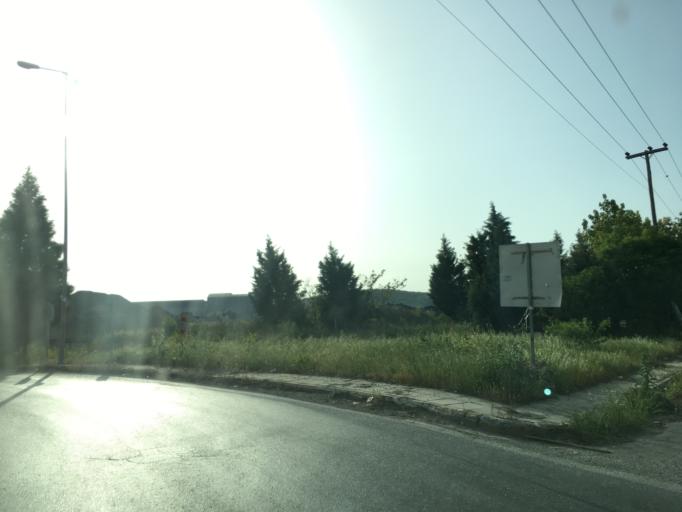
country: GR
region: Thessaly
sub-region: Nomos Magnisias
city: Velestino
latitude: 39.3861
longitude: 22.8133
